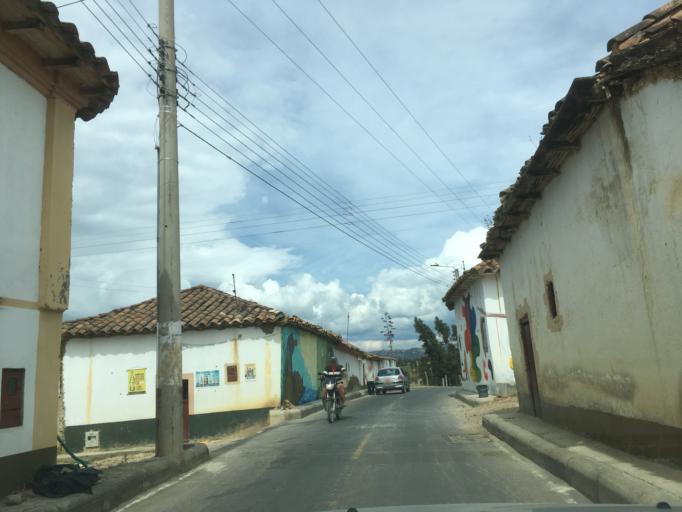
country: CO
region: Boyaca
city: Pesca
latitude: 5.5619
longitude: -72.9836
